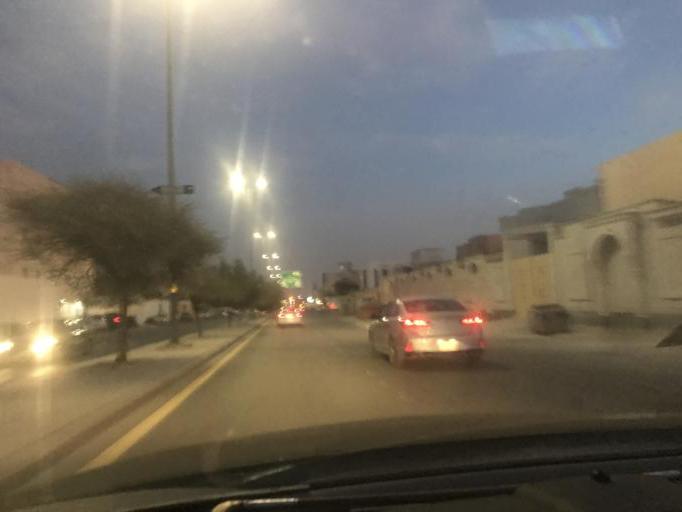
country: SA
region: Ar Riyad
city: Riyadh
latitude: 24.7337
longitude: 46.7601
